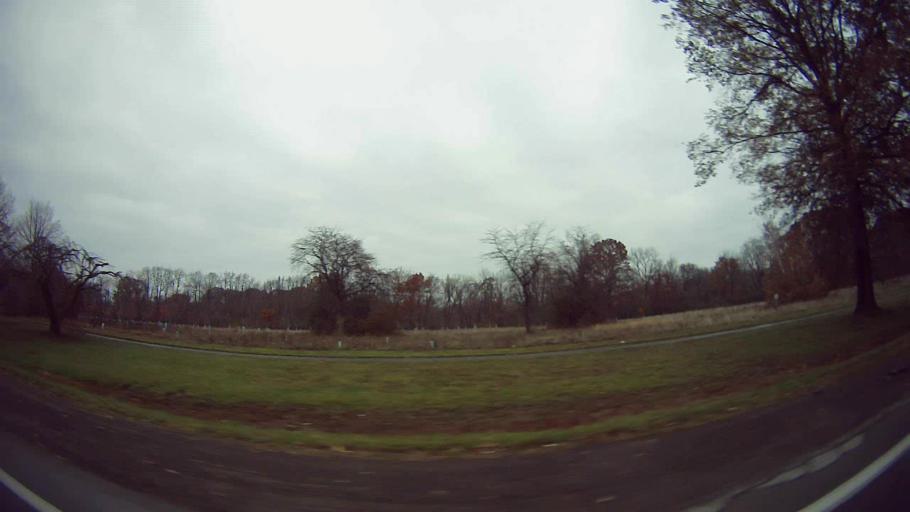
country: US
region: Michigan
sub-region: Wayne County
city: Dearborn Heights
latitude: 42.3583
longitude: -83.2629
